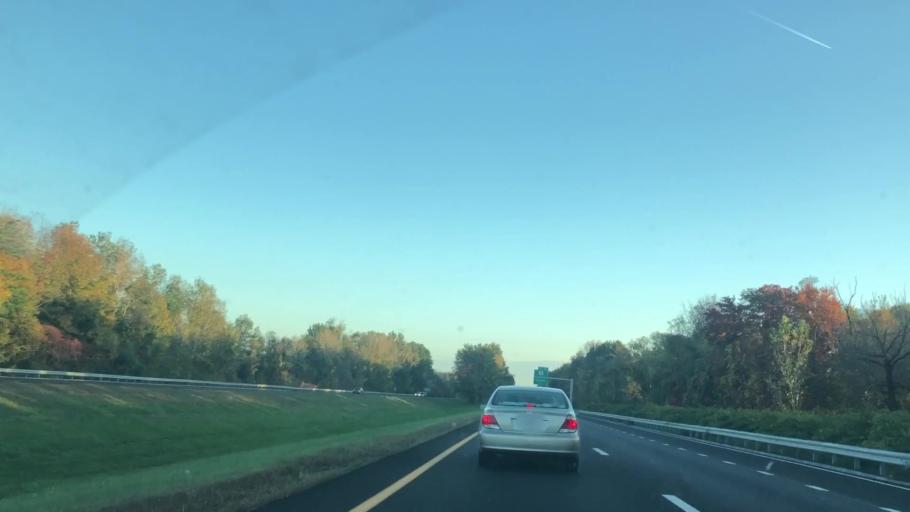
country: US
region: Massachusetts
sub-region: Franklin County
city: South Deerfield
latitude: 42.5026
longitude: -72.6196
